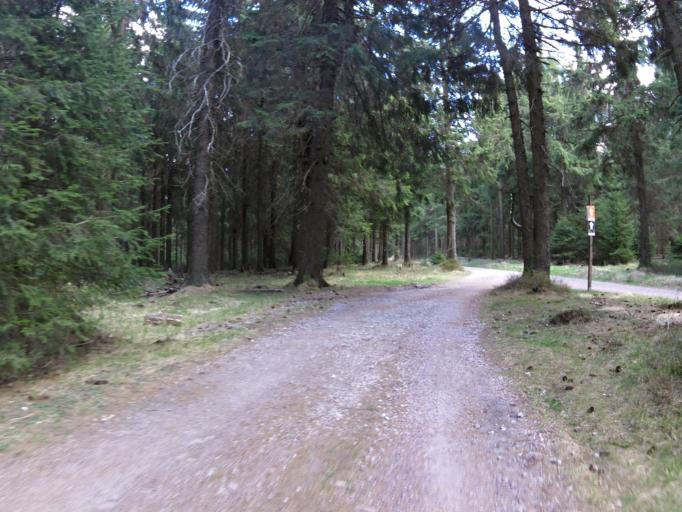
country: DE
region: Thuringia
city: Zella-Mehlis
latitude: 50.7097
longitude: 10.6660
